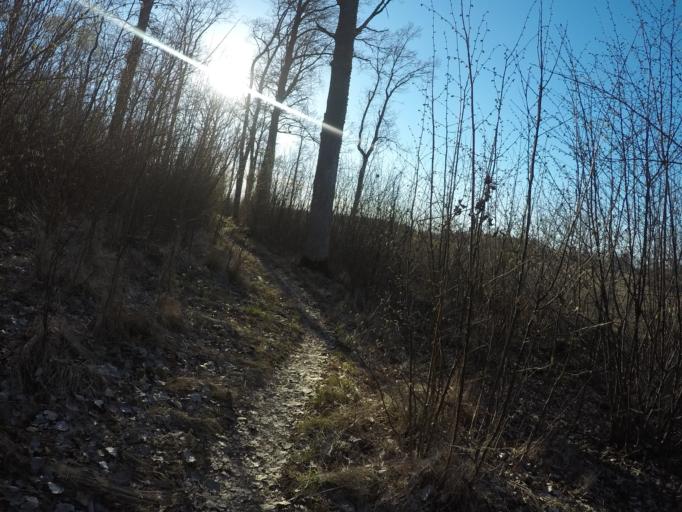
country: SE
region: Soedermanland
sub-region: Eskilstuna Kommun
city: Eskilstuna
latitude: 59.4058
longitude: 16.5135
